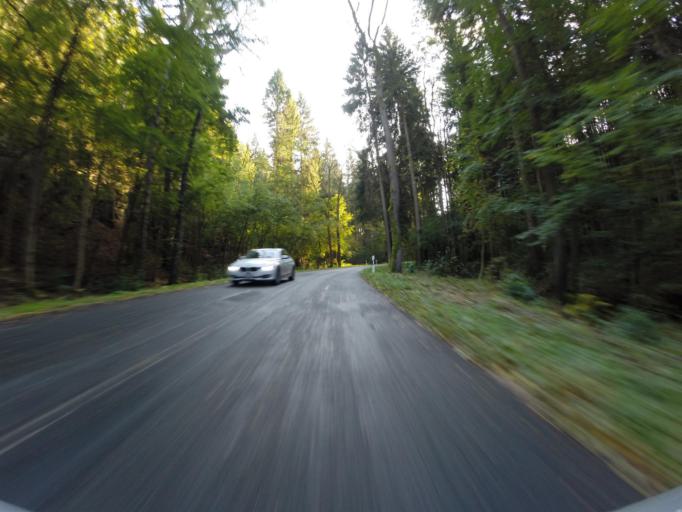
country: DE
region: Thuringia
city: Jena
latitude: 50.9332
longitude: 11.5397
